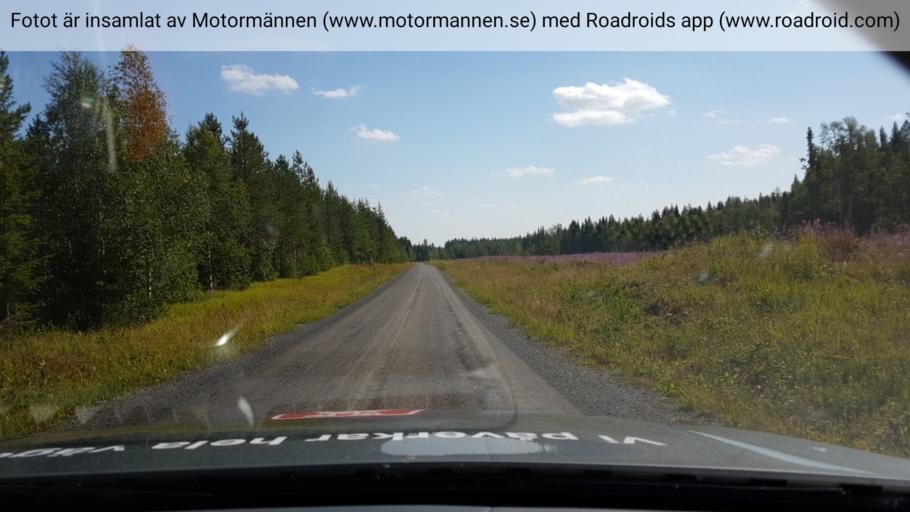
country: SE
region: Jaemtland
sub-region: OEstersunds Kommun
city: Lit
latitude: 63.3521
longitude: 15.2294
